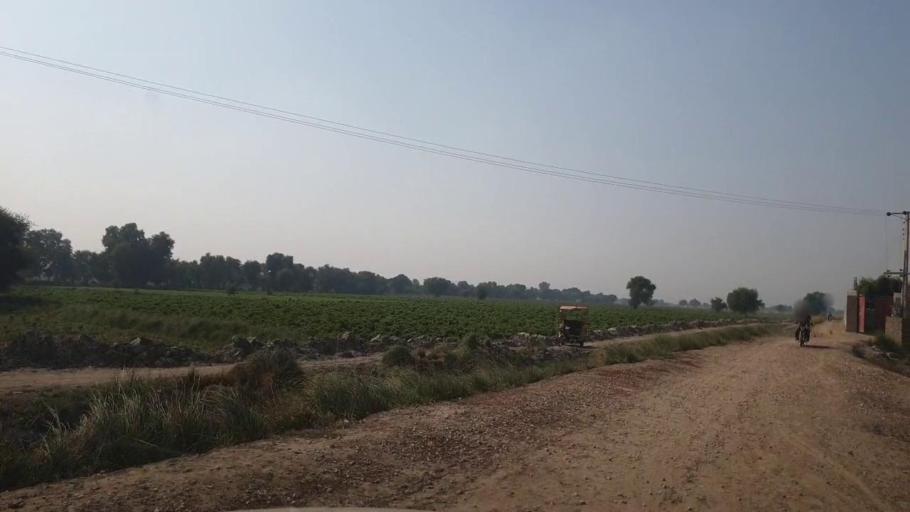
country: PK
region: Sindh
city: Bhan
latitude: 26.5291
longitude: 67.7781
